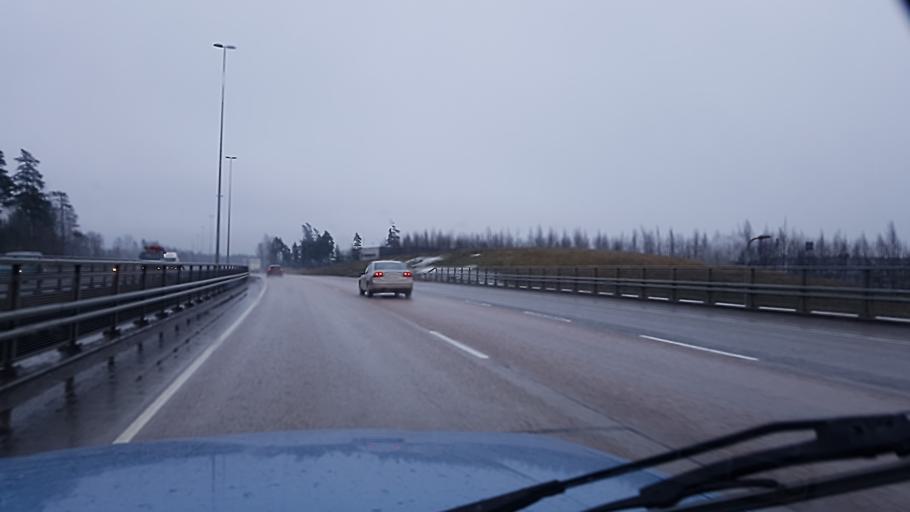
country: FI
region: Uusimaa
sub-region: Helsinki
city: Vantaa
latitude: 60.2970
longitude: 24.9161
